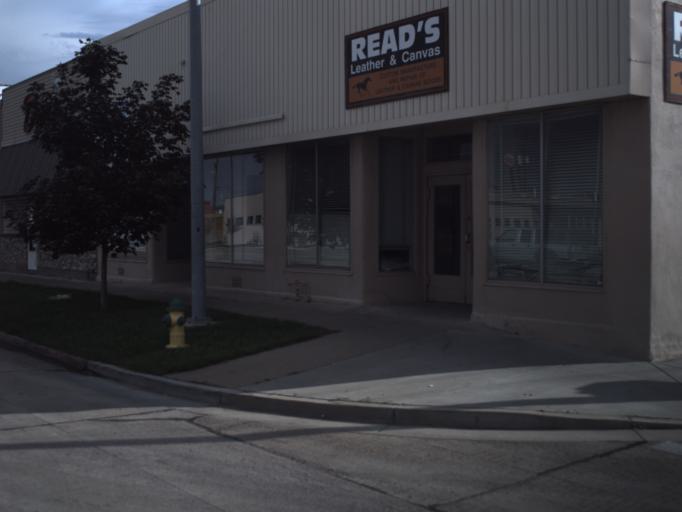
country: US
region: Utah
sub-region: Weber County
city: Harrisville
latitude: 41.2580
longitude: -111.9696
